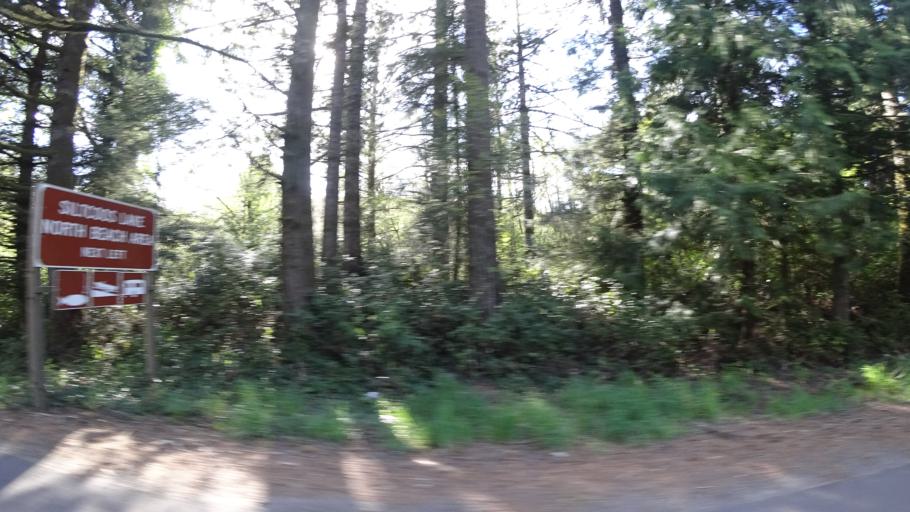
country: US
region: Oregon
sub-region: Lane County
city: Dunes City
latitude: 43.8989
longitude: -124.1169
